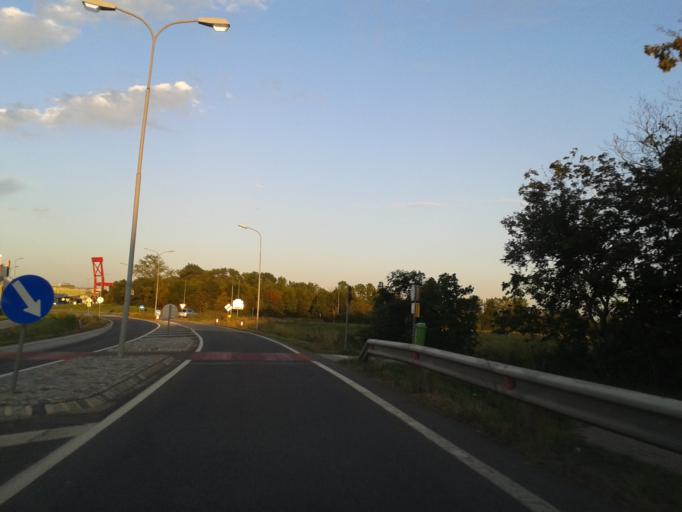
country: AT
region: Lower Austria
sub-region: Politischer Bezirk Modling
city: Wiener Neudorf
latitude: 48.1048
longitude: 16.3088
